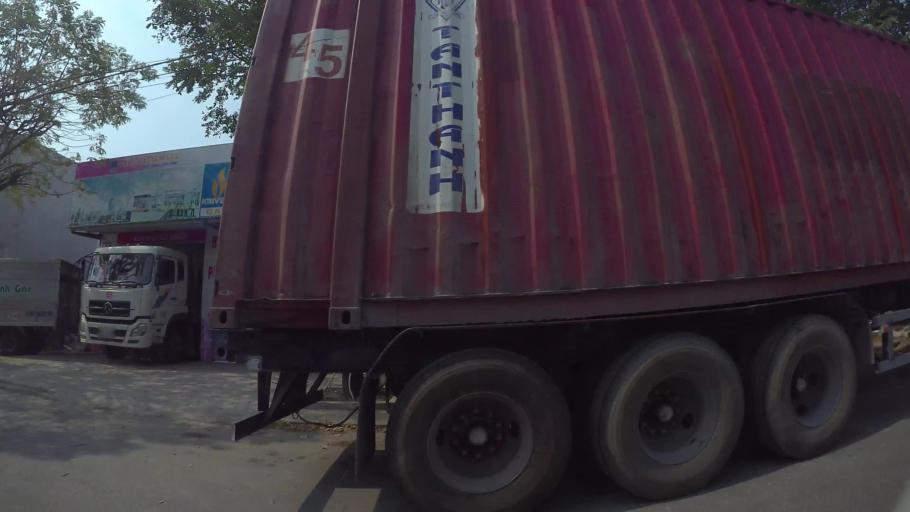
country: VN
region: Da Nang
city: Cam Le
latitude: 16.0024
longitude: 108.2249
